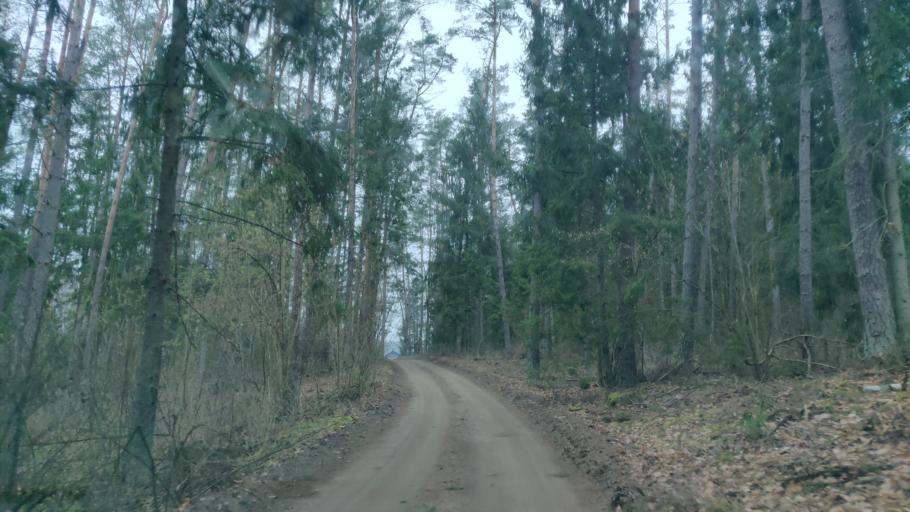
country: LT
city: Trakai
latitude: 54.5584
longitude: 24.9351
